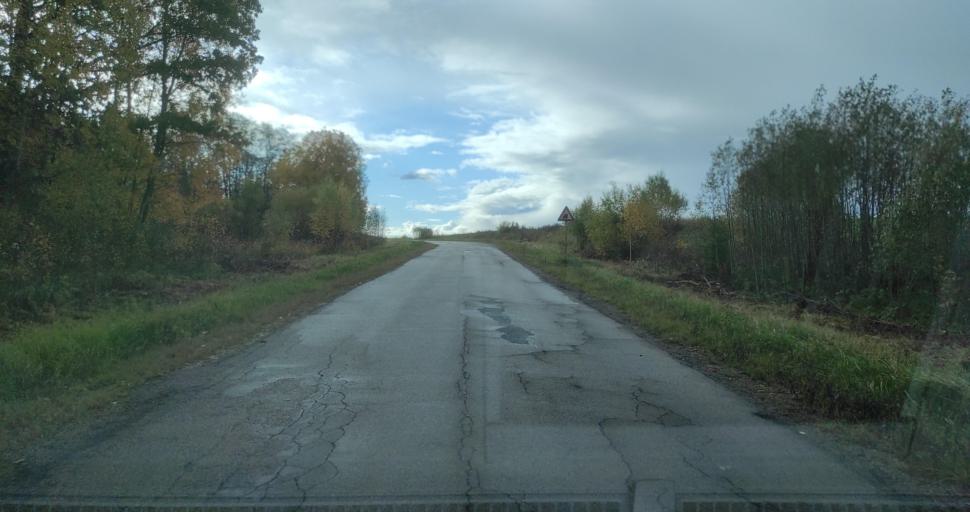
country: LV
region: Vainode
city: Vainode
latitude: 56.5613
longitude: 21.9065
